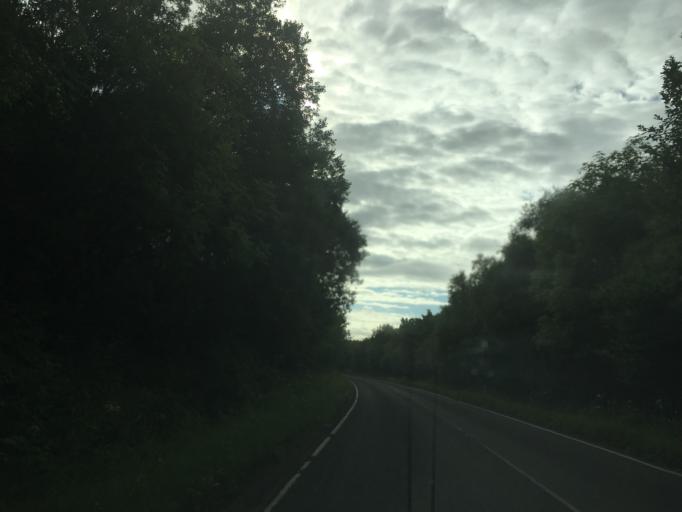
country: GB
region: Scotland
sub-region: Argyll and Bute
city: Oban
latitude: 56.3530
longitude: -5.4856
